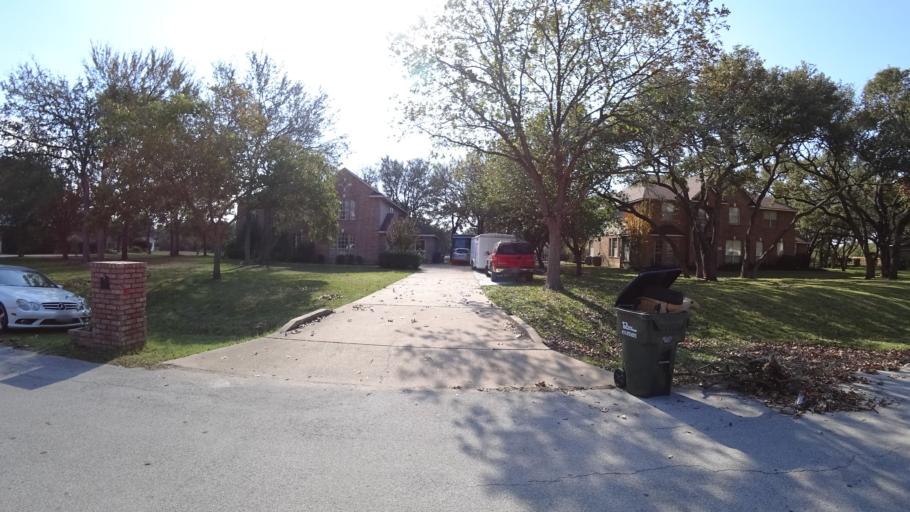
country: US
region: Texas
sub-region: Travis County
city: Shady Hollow
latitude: 30.1598
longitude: -97.8622
